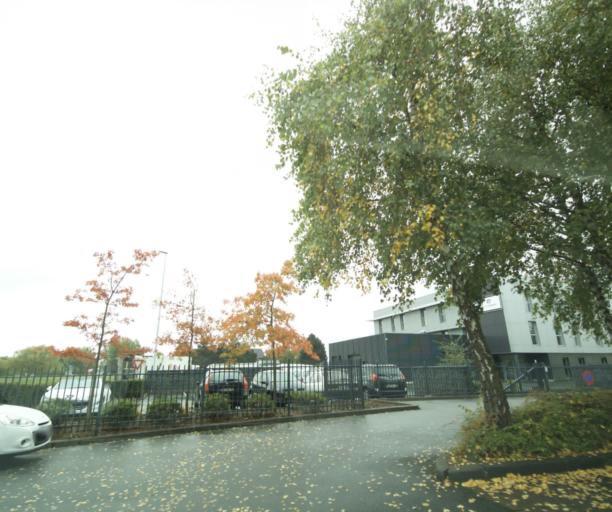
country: FR
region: Nord-Pas-de-Calais
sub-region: Departement du Nord
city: Neuville-en-Ferrain
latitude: 50.7558
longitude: 3.1398
